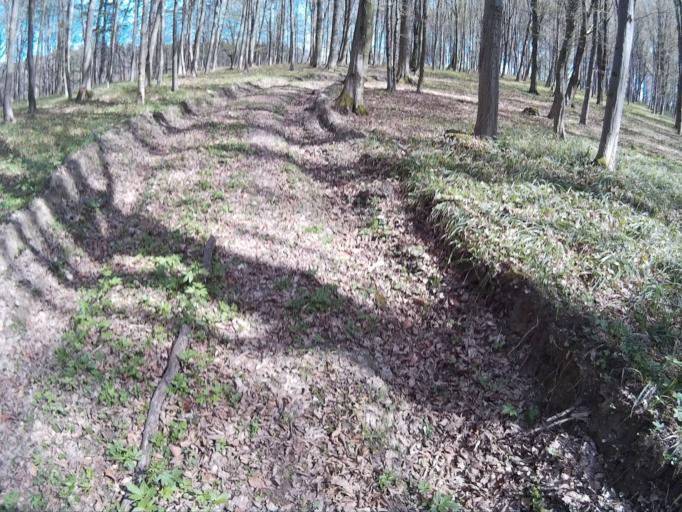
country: HU
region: Veszprem
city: Herend
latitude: 47.2062
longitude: 17.7769
